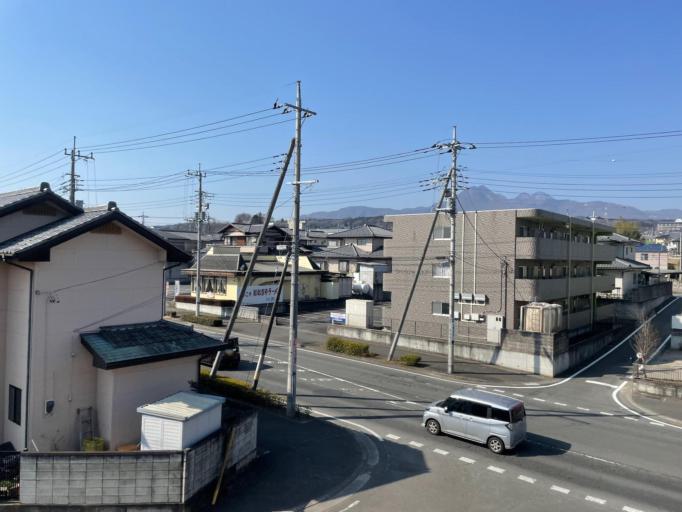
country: JP
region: Gunma
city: Shibukawa
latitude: 36.5030
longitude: 139.0045
